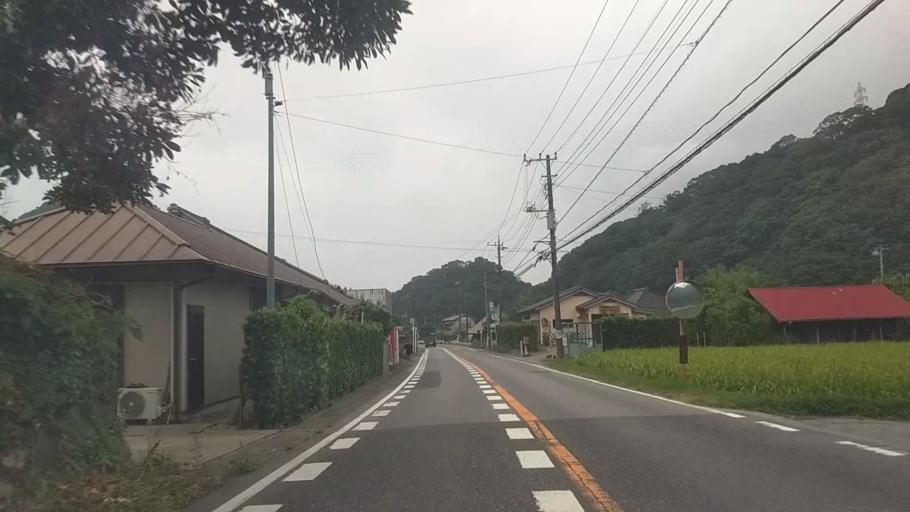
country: JP
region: Chiba
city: Tateyama
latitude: 35.1433
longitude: 139.8766
